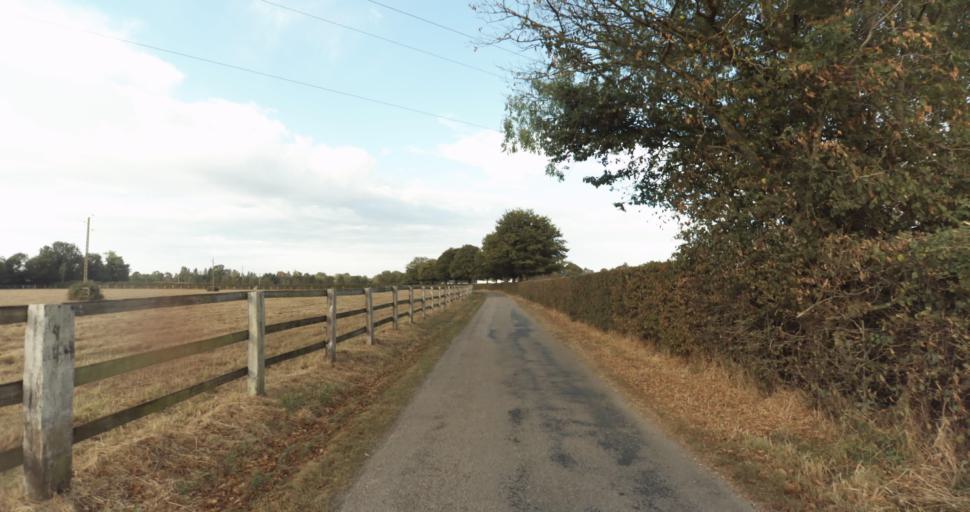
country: FR
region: Lower Normandy
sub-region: Departement de l'Orne
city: Vimoutiers
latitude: 48.9340
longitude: 0.2420
